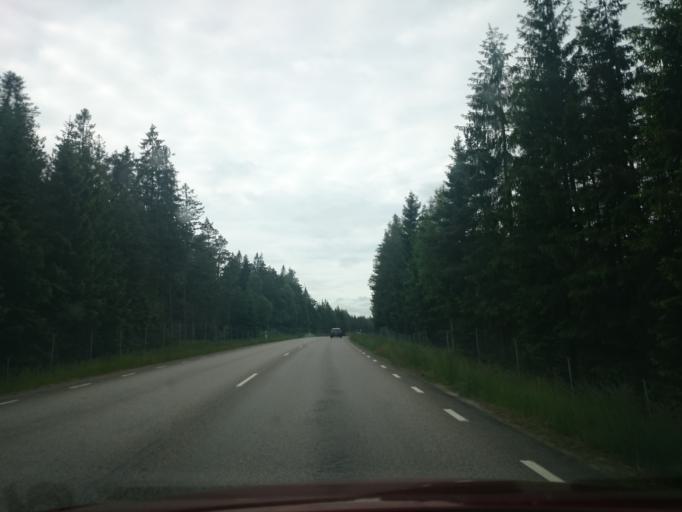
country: SE
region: Vaestra Goetaland
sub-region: Harryda Kommun
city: Hindas
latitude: 57.6877
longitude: 12.3705
